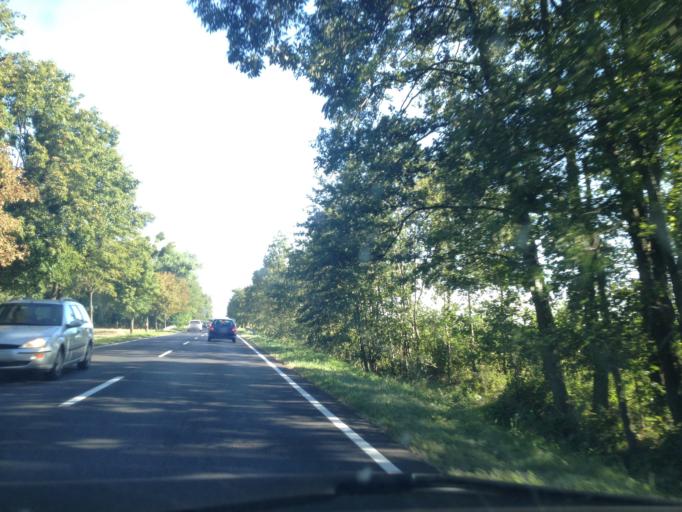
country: PL
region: Greater Poland Voivodeship
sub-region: Powiat sremski
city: Srem
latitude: 52.1375
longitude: 17.0402
